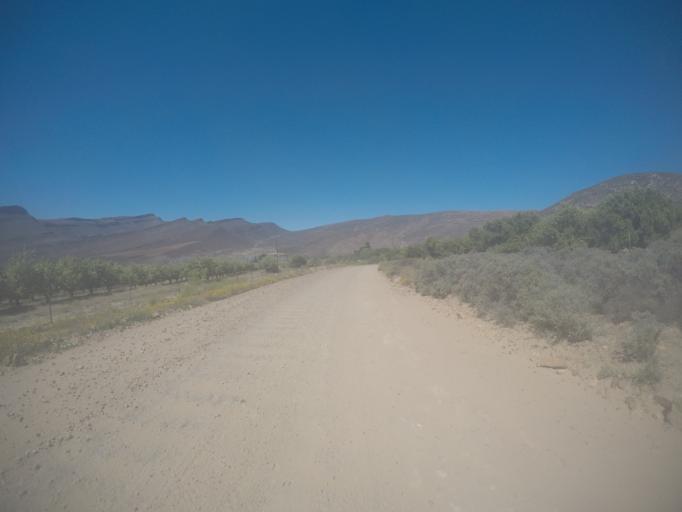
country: ZA
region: Western Cape
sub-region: West Coast District Municipality
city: Clanwilliam
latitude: -32.5592
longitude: 19.3615
